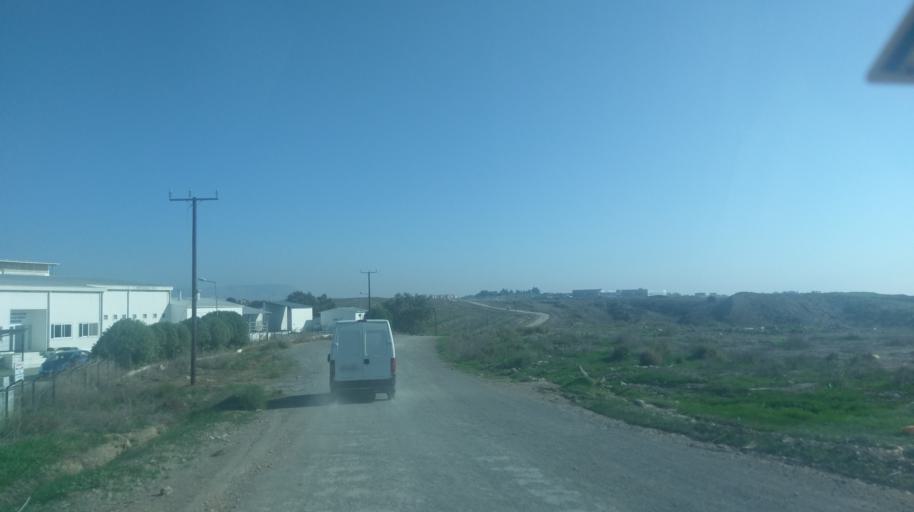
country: CY
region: Lefkosia
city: Nicosia
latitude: 35.2220
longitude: 33.3531
